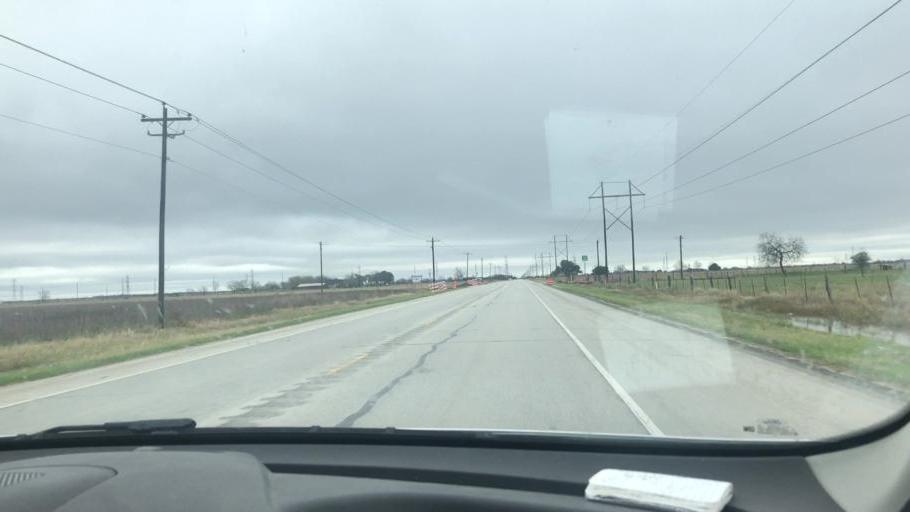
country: US
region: Texas
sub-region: Wharton County
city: Boling
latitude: 29.1870
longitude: -96.0122
